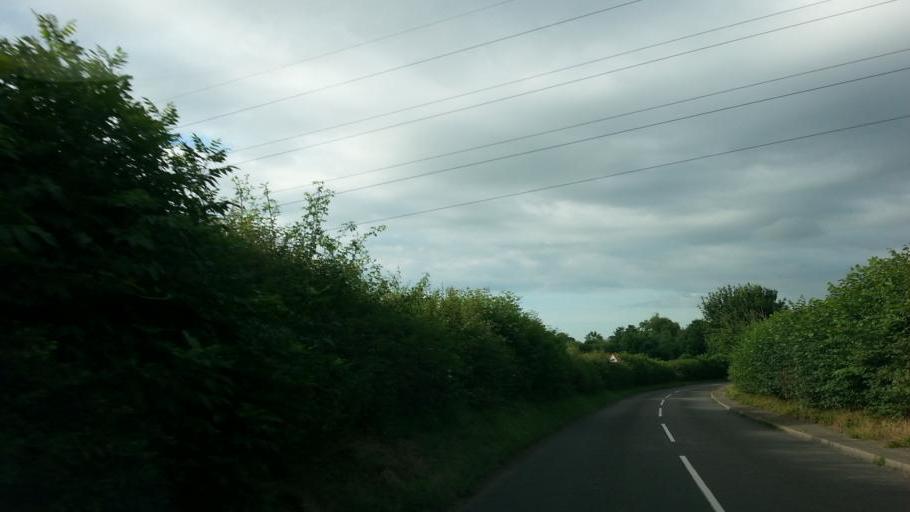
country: GB
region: England
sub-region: Nottinghamshire
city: Newark on Trent
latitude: 53.0576
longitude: -0.8265
